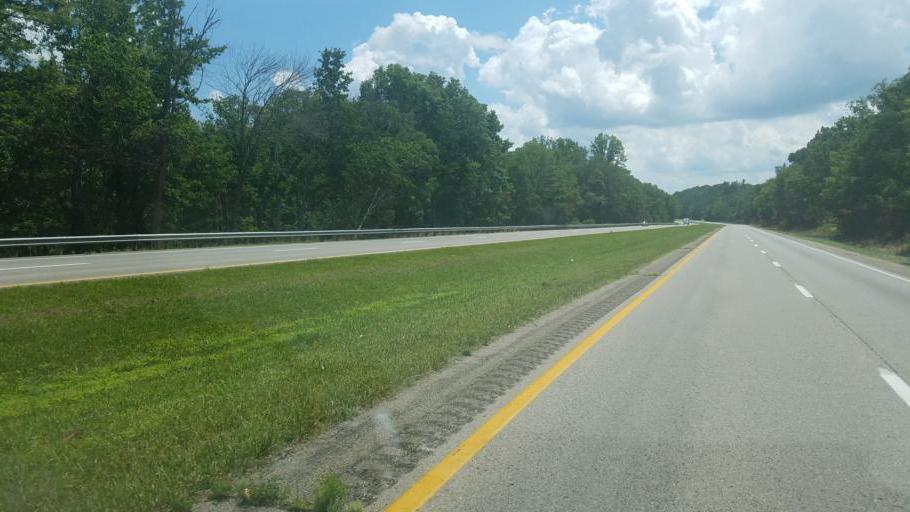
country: US
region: Ohio
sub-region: Jackson County
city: Jackson
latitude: 39.0069
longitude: -82.5669
